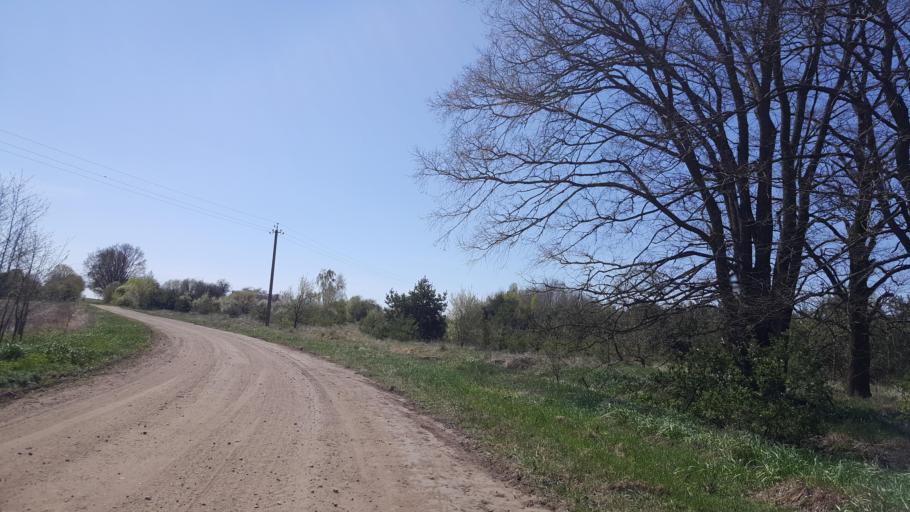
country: BY
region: Brest
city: Kamyanyets
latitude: 52.3295
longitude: 23.7389
